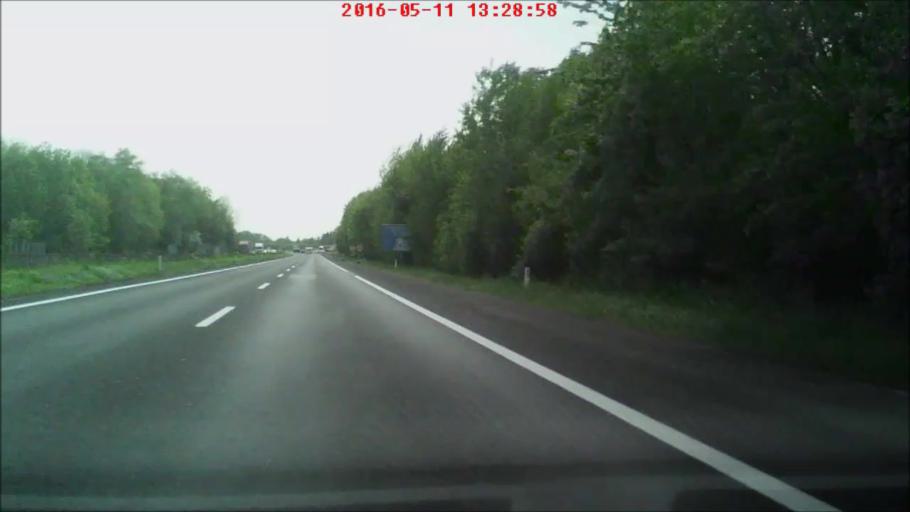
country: AT
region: Upper Austria
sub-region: Politischer Bezirk Scharding
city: Sankt Marienkirchen bei Schaerding
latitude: 48.3795
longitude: 13.4170
